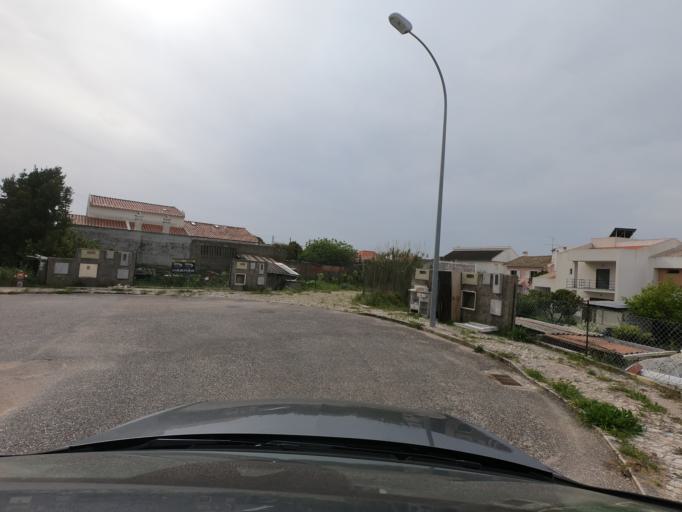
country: PT
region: Lisbon
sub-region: Oeiras
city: Porto Salvo
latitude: 38.7200
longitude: -9.2920
